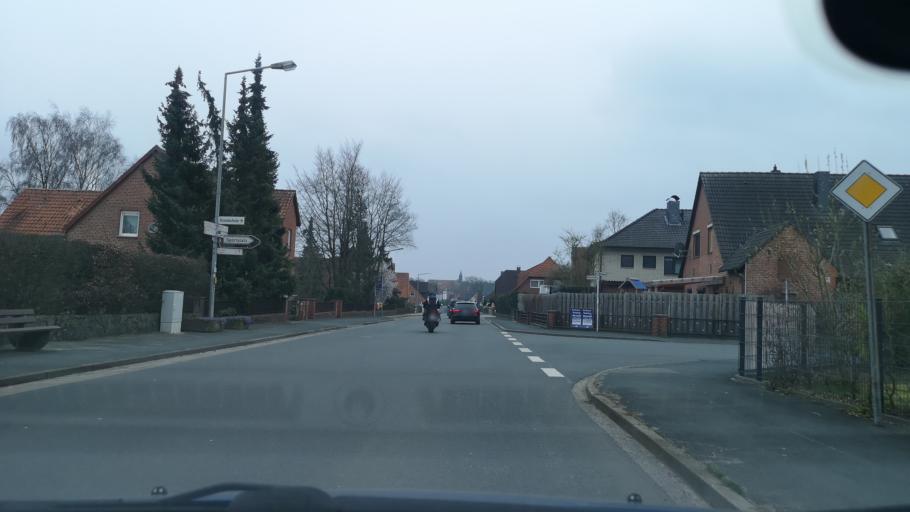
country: DE
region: Lower Saxony
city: Neustadt am Rubenberge
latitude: 52.5644
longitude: 9.4872
